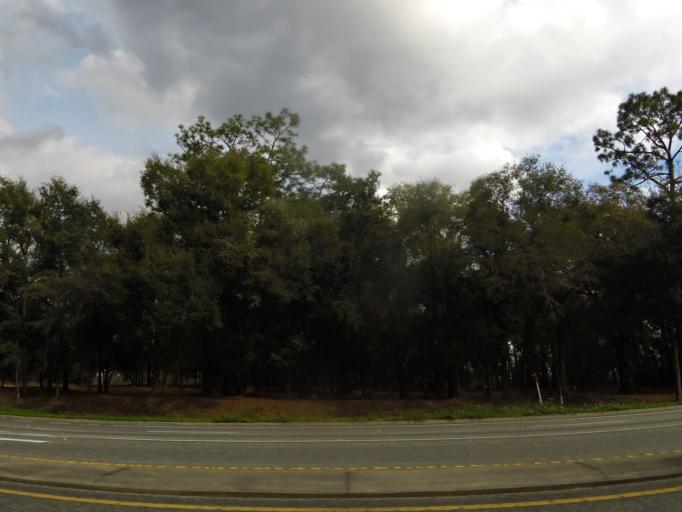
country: US
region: Florida
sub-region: Volusia County
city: De Leon Springs
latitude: 29.0860
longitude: -81.3257
